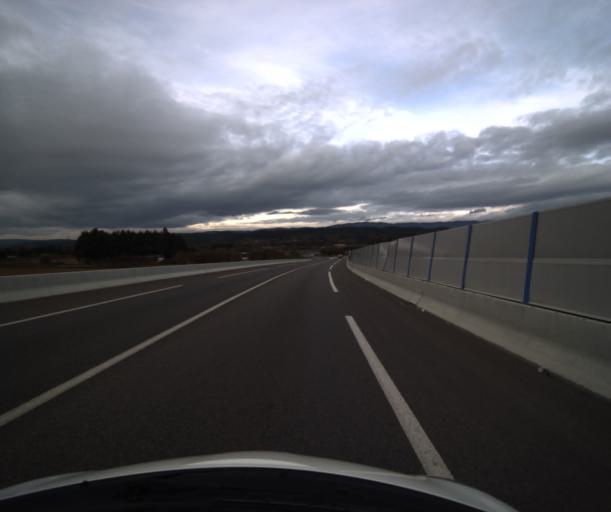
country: FR
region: Provence-Alpes-Cote d'Azur
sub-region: Departement du Vaucluse
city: Pertuis
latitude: 43.6848
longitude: 5.4839
